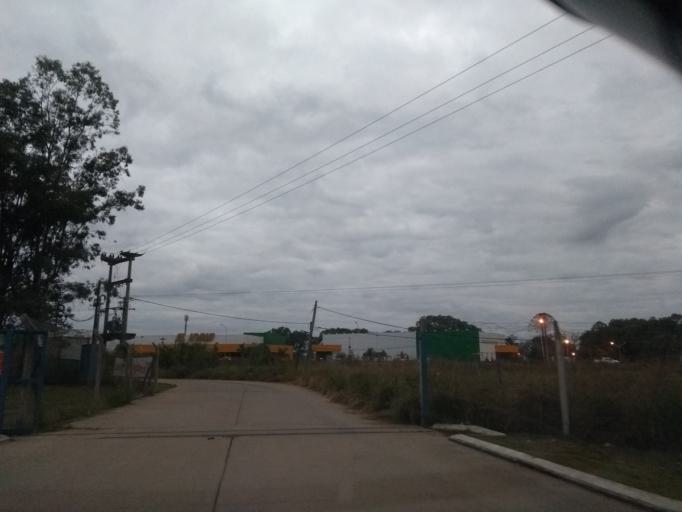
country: AR
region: Chaco
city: Fontana
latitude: -27.4092
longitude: -59.0026
